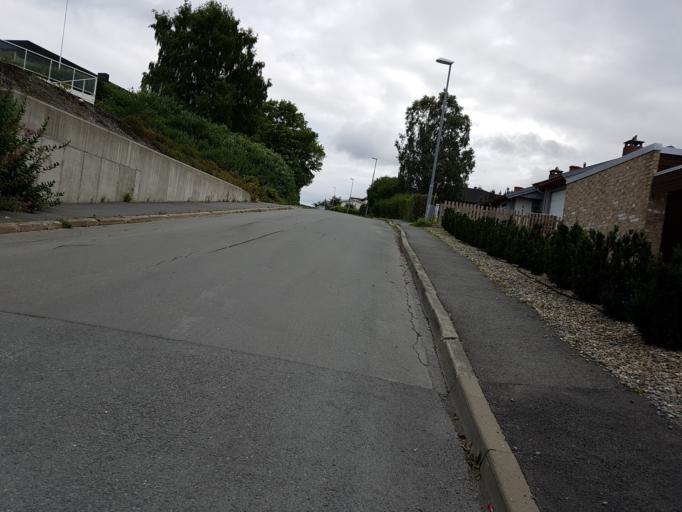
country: NO
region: Sor-Trondelag
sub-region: Trondheim
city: Trondheim
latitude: 63.3956
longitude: 10.4171
